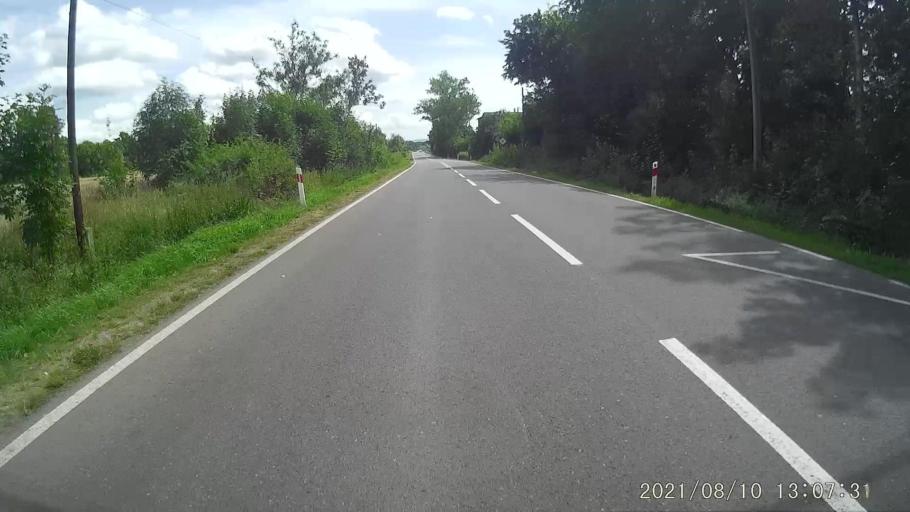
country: PL
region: Lower Silesian Voivodeship
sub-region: Powiat klodzki
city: Bozkow
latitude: 50.4887
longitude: 16.5718
